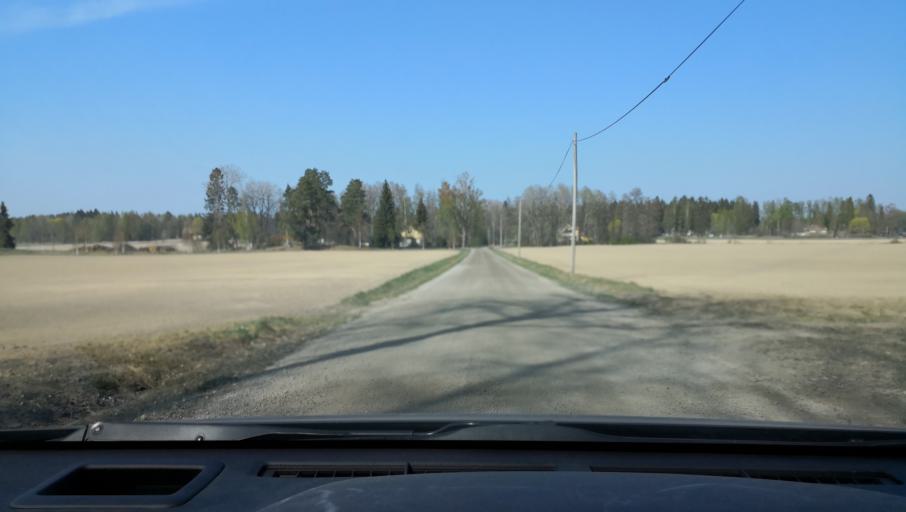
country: SE
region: Uppsala
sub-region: Heby Kommun
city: Heby
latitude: 60.0322
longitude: 16.7822
